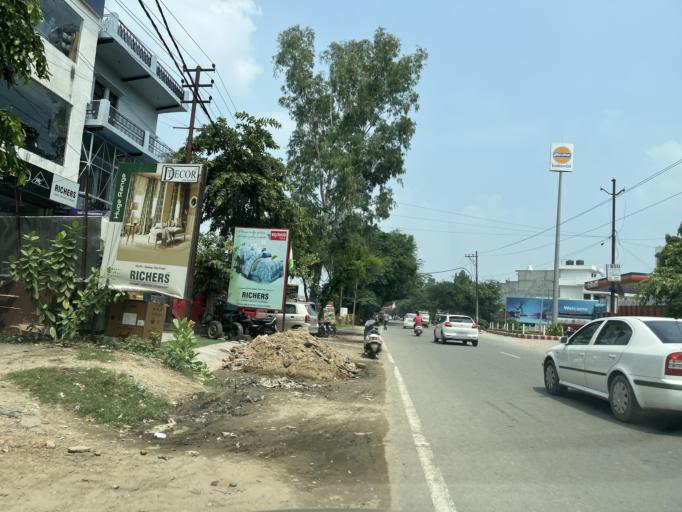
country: IN
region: Uttar Pradesh
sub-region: Bijnor
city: Najibabad
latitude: 29.5949
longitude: 78.3392
